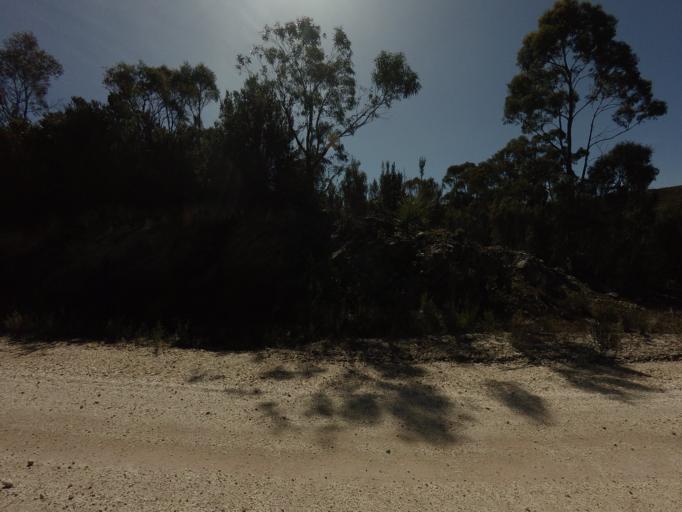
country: AU
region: Tasmania
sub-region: Huon Valley
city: Geeveston
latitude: -43.0323
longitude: 146.3078
